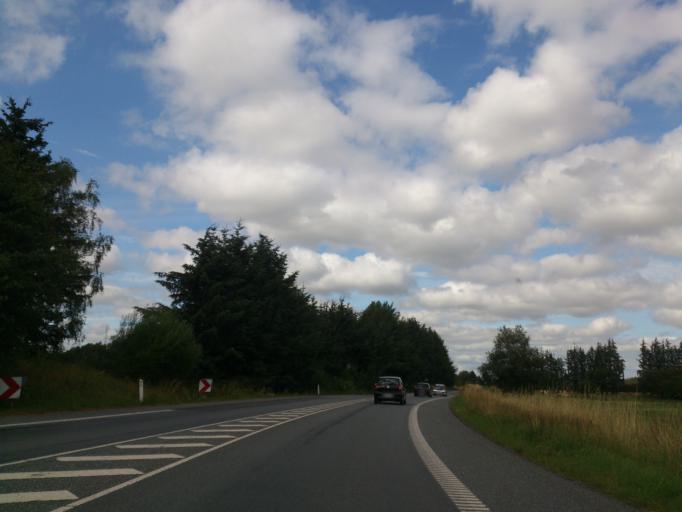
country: DK
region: South Denmark
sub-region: Aabenraa Kommune
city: Krusa
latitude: 54.8683
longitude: 9.4051
